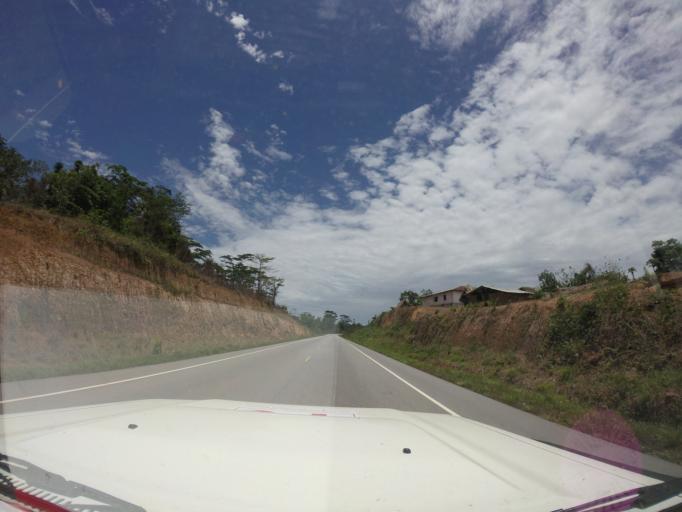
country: LR
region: Bong
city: Gbarnga
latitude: 6.8354
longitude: -9.8536
